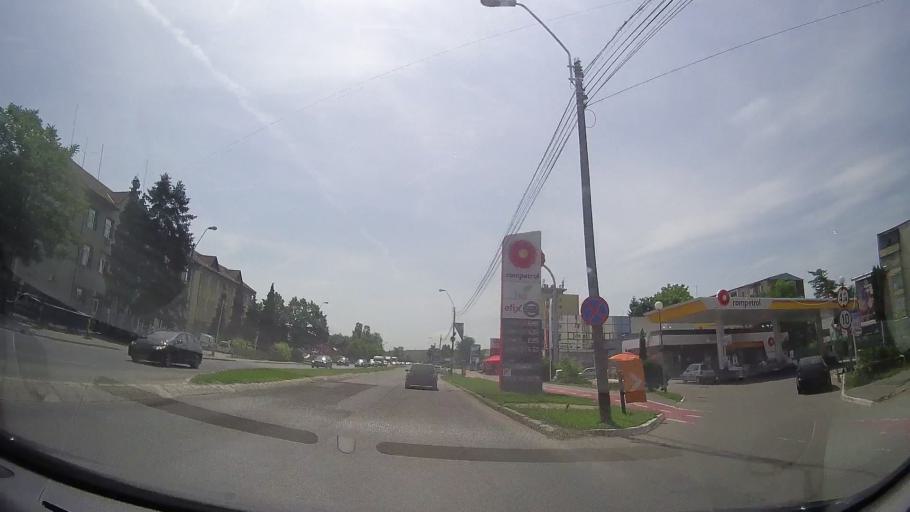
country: RO
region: Hunedoara
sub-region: Municipiul Deva
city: Deva
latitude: 45.8767
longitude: 22.9152
